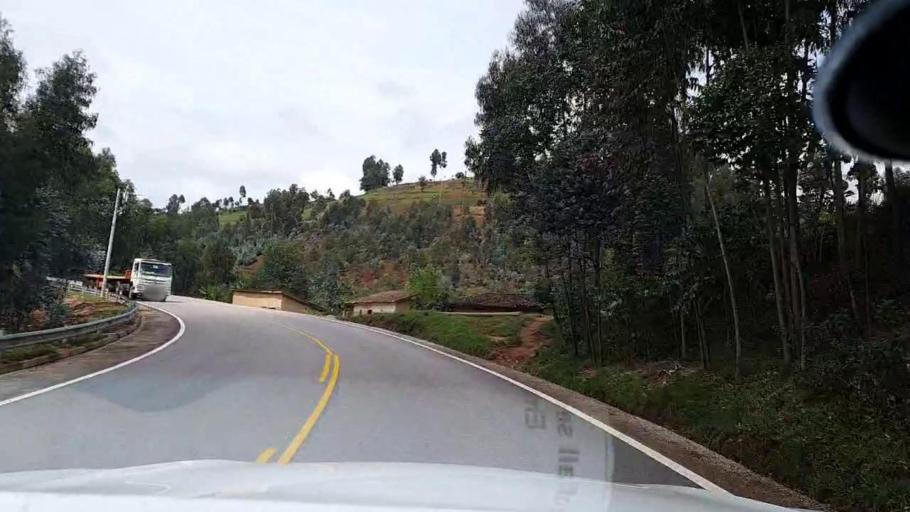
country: RW
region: Southern Province
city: Nzega
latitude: -2.5143
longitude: 29.4611
